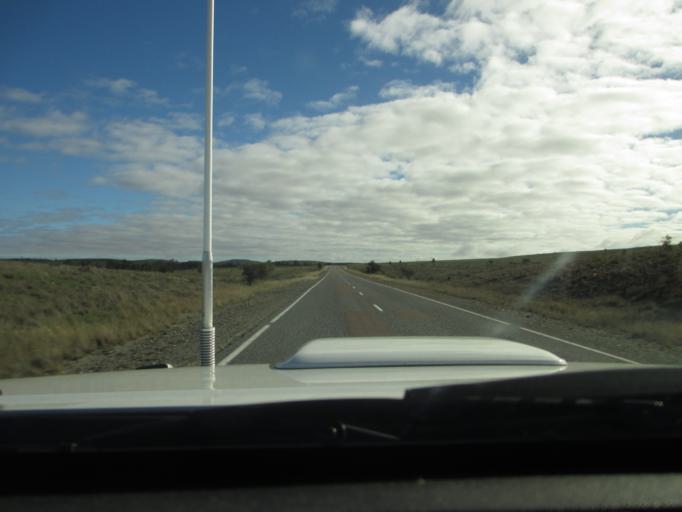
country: AU
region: South Australia
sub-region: Peterborough
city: Peterborough
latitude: -32.5946
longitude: 138.5630
